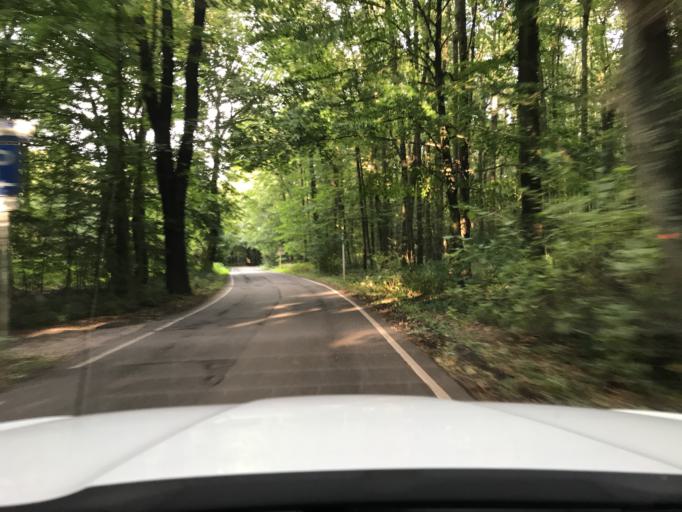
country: DE
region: North Rhine-Westphalia
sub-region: Regierungsbezirk Dusseldorf
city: Duisburg
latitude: 51.4062
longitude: 6.8194
